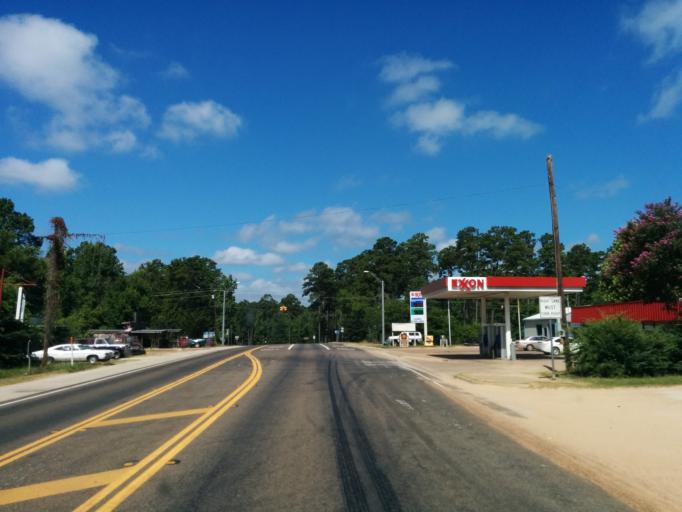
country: US
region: Texas
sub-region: Houston County
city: Hickory Creek
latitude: 31.3918
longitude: -95.1388
